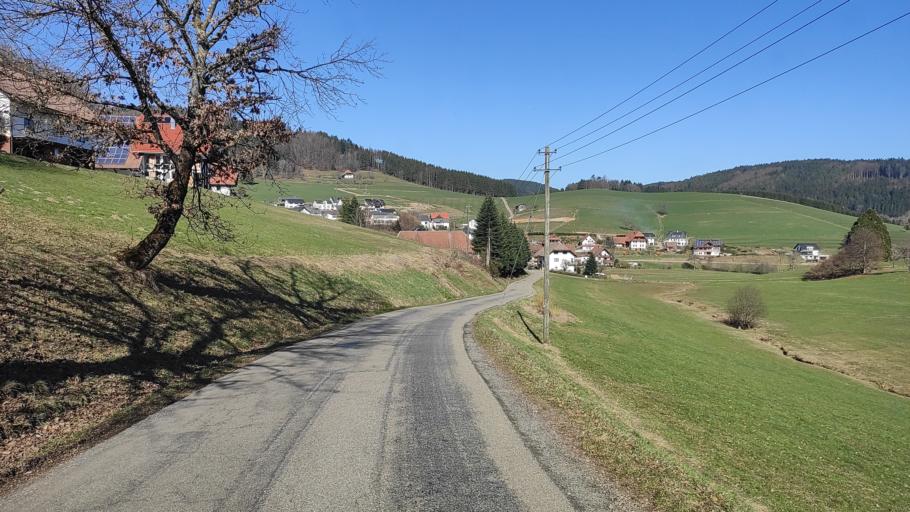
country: DE
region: Baden-Wuerttemberg
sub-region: Freiburg Region
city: Elzach
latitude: 48.1905
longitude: 8.0321
